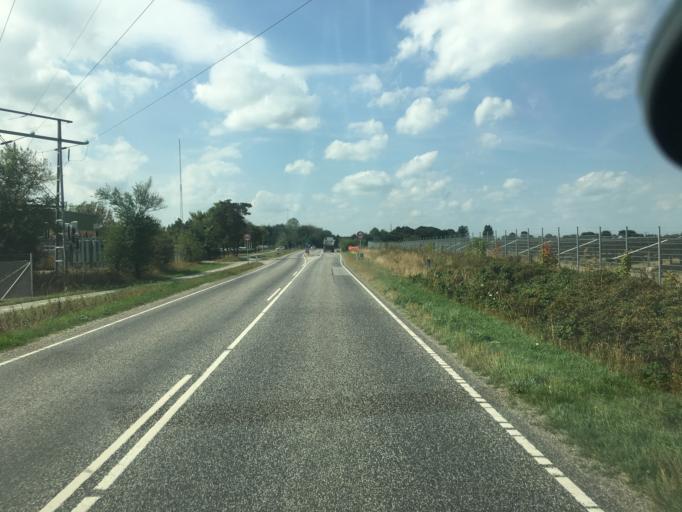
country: DK
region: South Denmark
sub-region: Aabenraa Kommune
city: Tinglev
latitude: 54.9426
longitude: 9.2670
